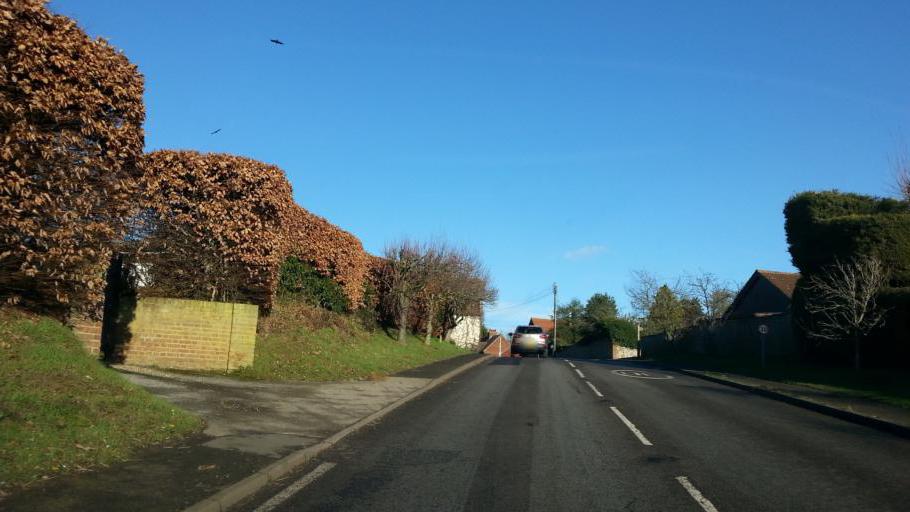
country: GB
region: England
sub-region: Suffolk
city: Saxmundham
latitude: 52.1701
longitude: 1.5004
